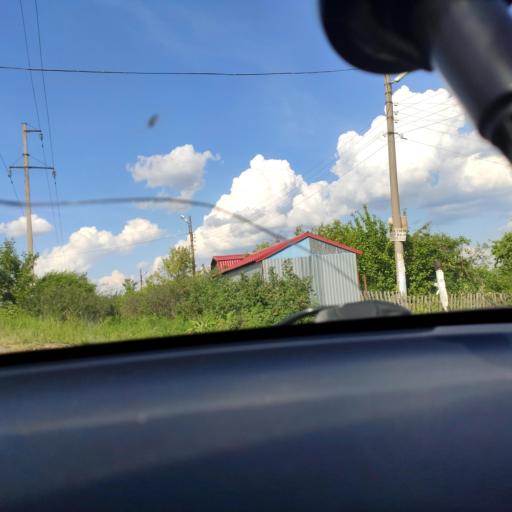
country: RU
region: Tatarstan
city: Verkhniy Uslon
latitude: 55.6486
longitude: 48.9443
